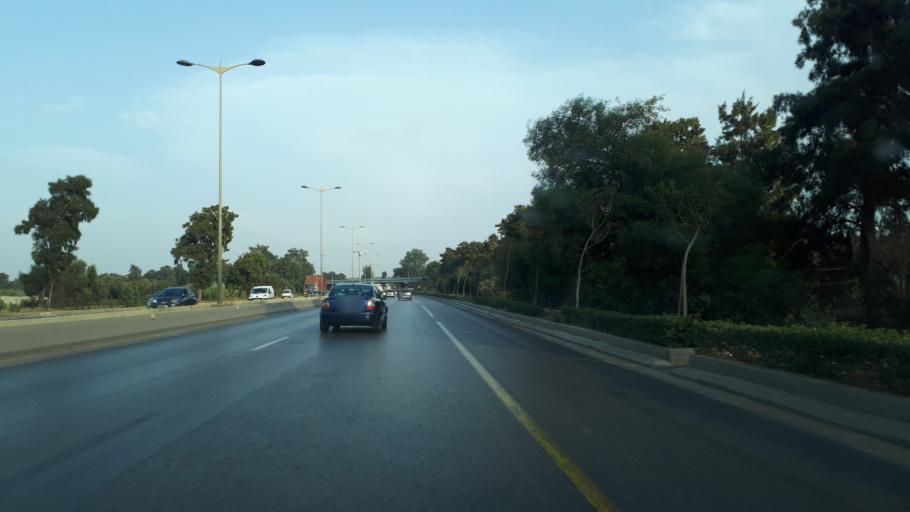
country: DZ
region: Alger
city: Dar el Beida
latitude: 36.7292
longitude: 3.2078
